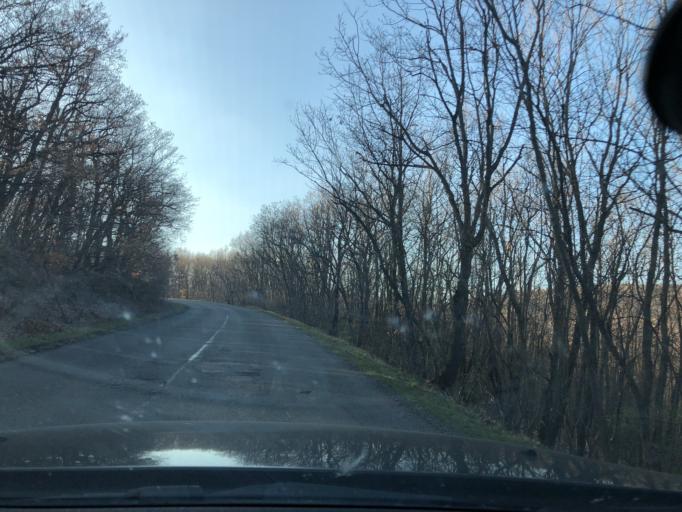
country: HU
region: Nograd
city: Paszto
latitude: 47.9173
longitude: 19.6369
